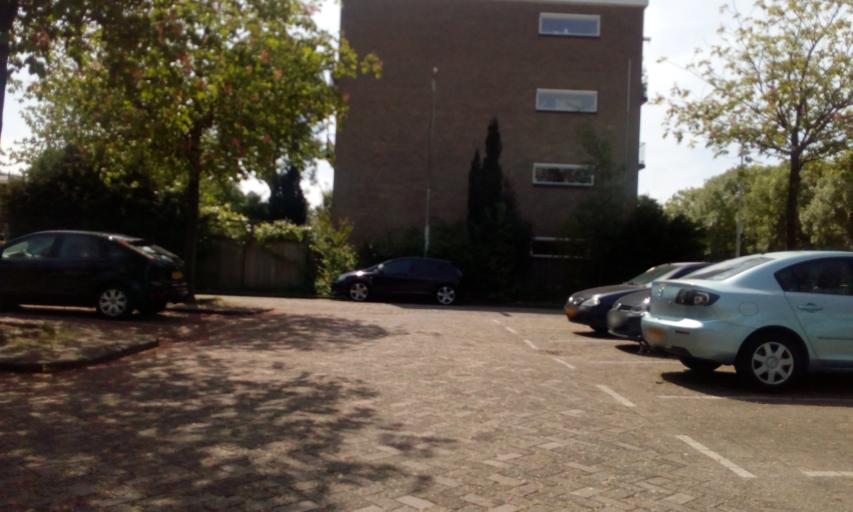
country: NL
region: South Holland
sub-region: Gemeente Rotterdam
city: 's-Gravenland
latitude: 51.9453
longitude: 4.5350
